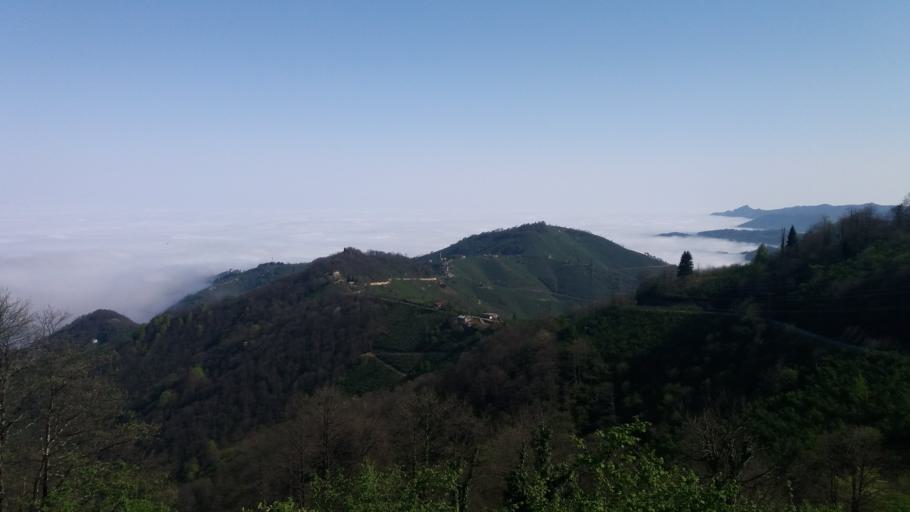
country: TR
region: Ordu
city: Kabaduz
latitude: 40.8232
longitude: 37.9042
